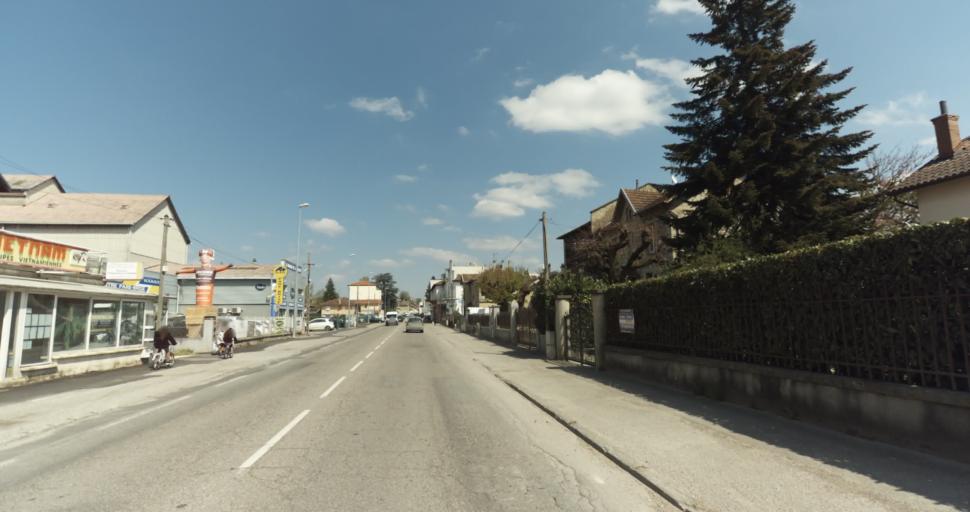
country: FR
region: Rhone-Alpes
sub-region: Departement de l'Isere
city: Saint-Marcellin
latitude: 45.1489
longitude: 5.3140
